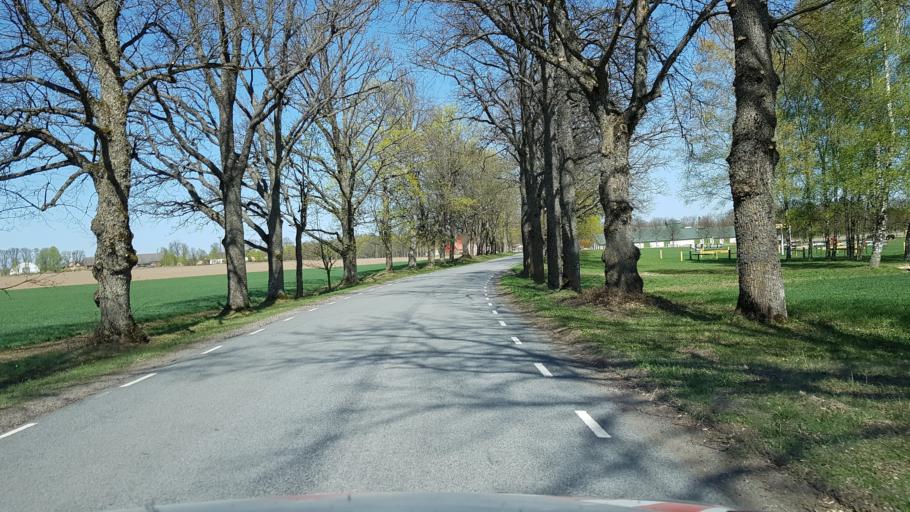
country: EE
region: Viljandimaa
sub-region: Vohma linn
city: Vohma
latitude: 58.5477
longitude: 25.5666
